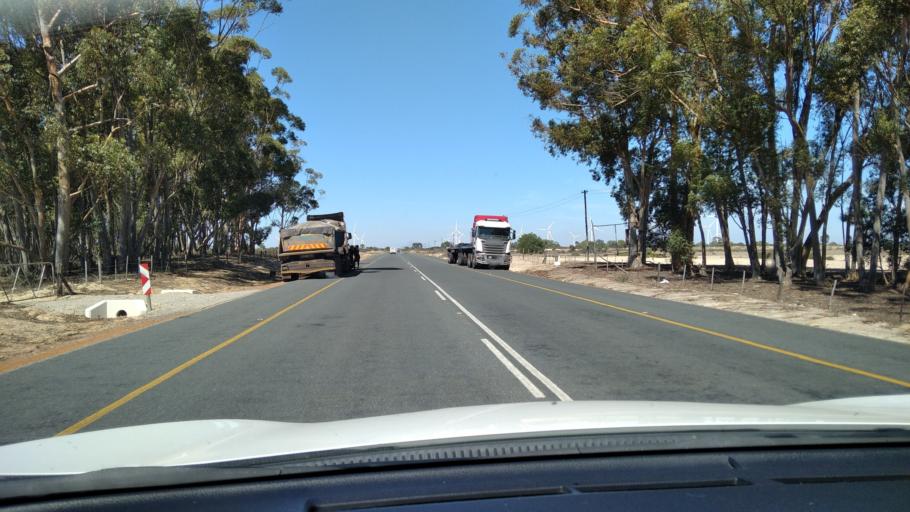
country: ZA
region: Western Cape
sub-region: West Coast District Municipality
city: Moorreesburg
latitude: -33.0662
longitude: 18.3640
